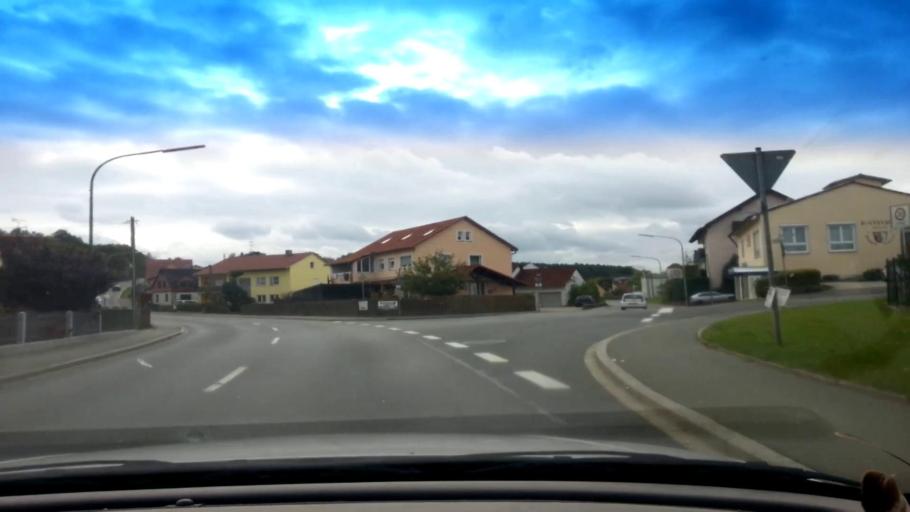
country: DE
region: Bavaria
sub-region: Upper Franconia
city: Oberhaid
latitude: 49.9119
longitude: 10.8035
